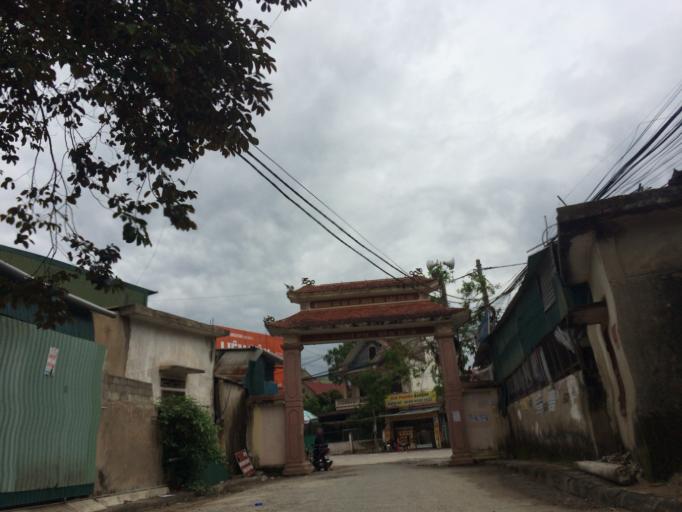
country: VN
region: Ha Tinh
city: Ha Tinh
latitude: 18.3413
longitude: 105.8868
